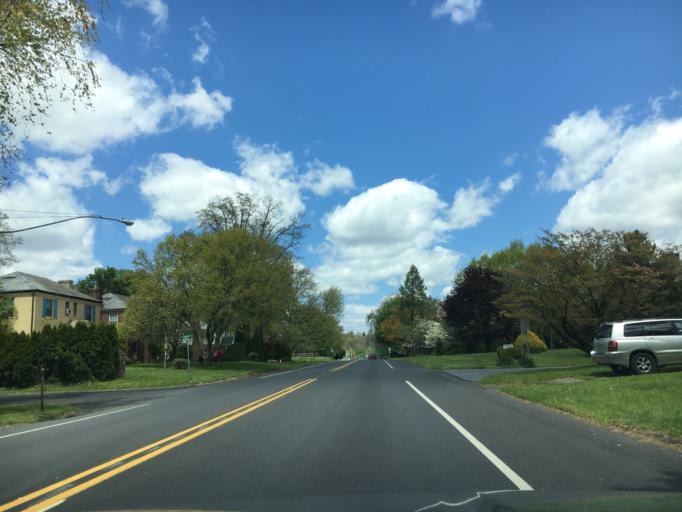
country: US
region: Pennsylvania
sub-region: Lehigh County
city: Dorneyville
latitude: 40.6066
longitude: -75.5306
